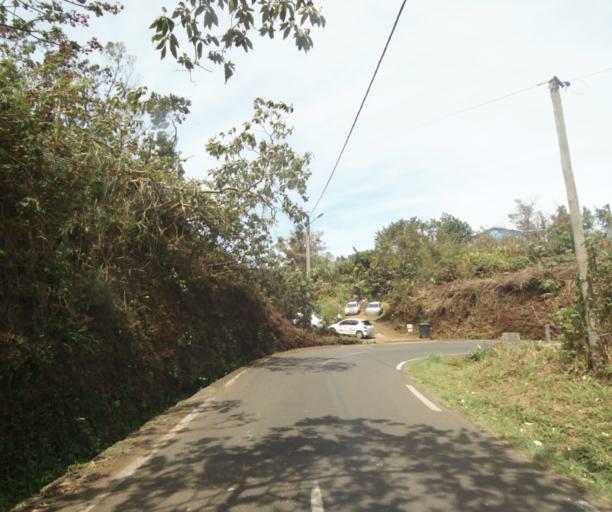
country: RE
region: Reunion
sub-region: Reunion
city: Trois-Bassins
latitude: -21.0658
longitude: 55.3082
